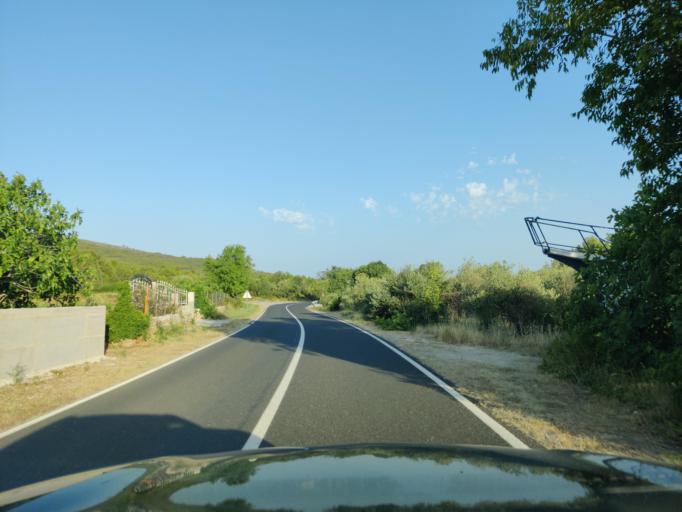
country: HR
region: Sibensko-Kniniska
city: Tribunj
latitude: 43.7720
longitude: 15.7257
